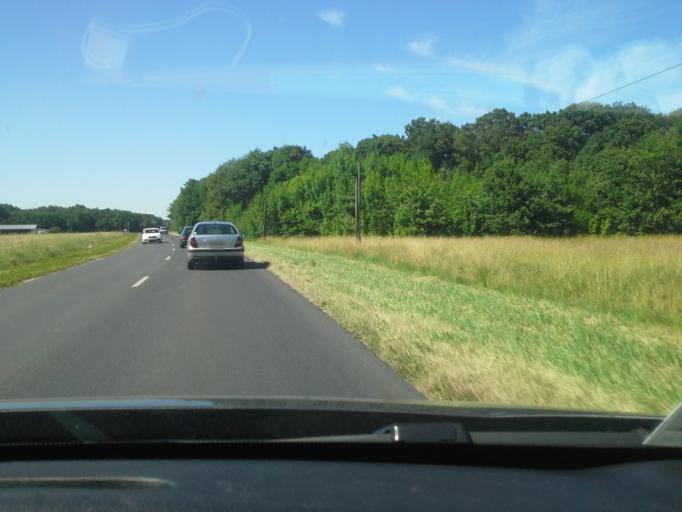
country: FR
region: Centre
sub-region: Departement du Loir-et-Cher
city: Cormeray
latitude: 47.5045
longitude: 1.4049
